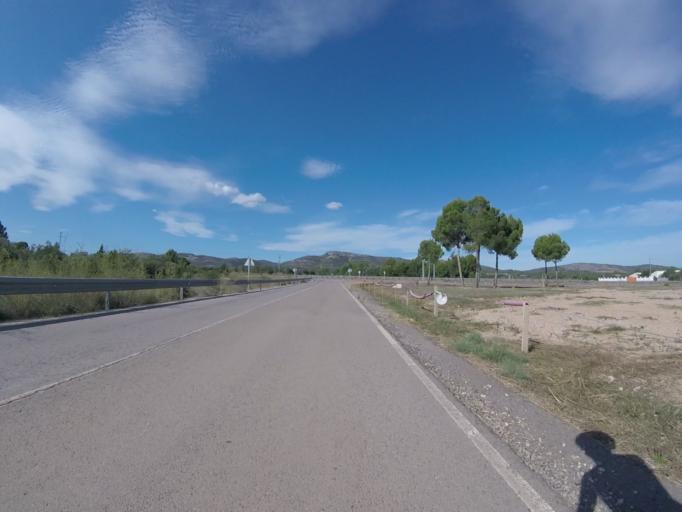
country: ES
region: Valencia
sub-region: Provincia de Castello
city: Peniscola
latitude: 40.3966
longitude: 0.3638
